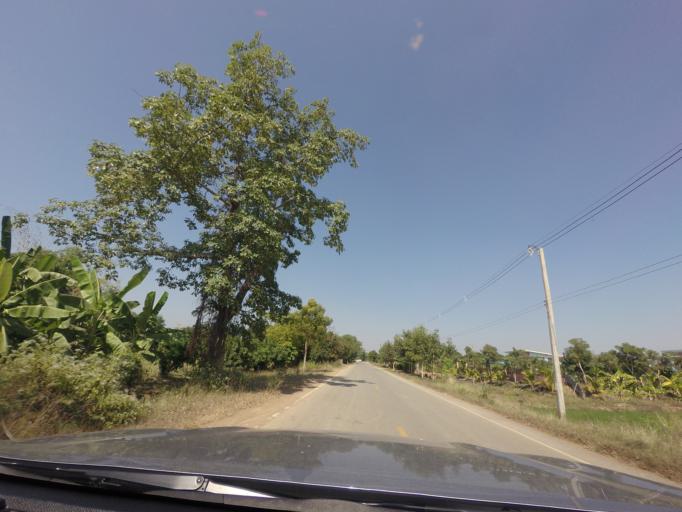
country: TH
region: Sukhothai
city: Si Samrong
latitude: 17.1573
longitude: 99.7705
